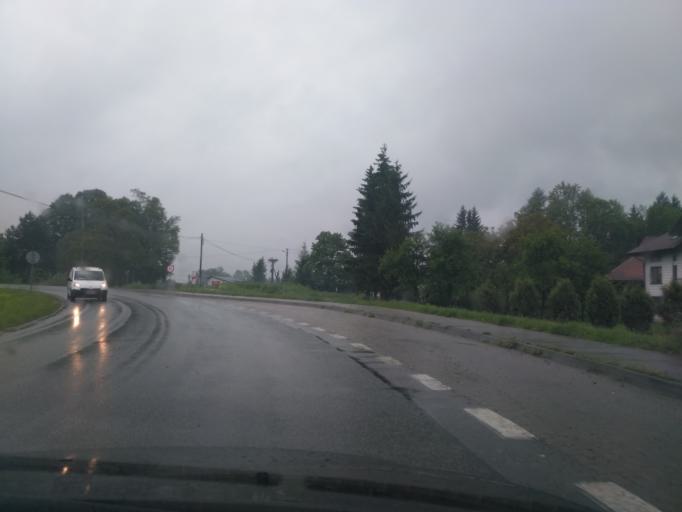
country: PL
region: Subcarpathian Voivodeship
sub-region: Powiat krosnienski
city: Leki
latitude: 49.7929
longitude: 21.6532
